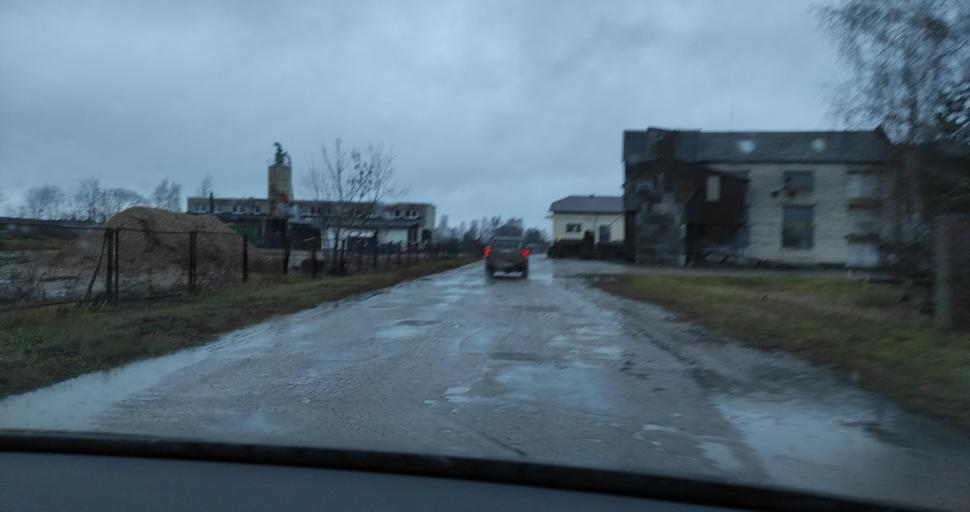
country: LV
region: Skrunda
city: Skrunda
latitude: 56.6701
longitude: 22.2197
